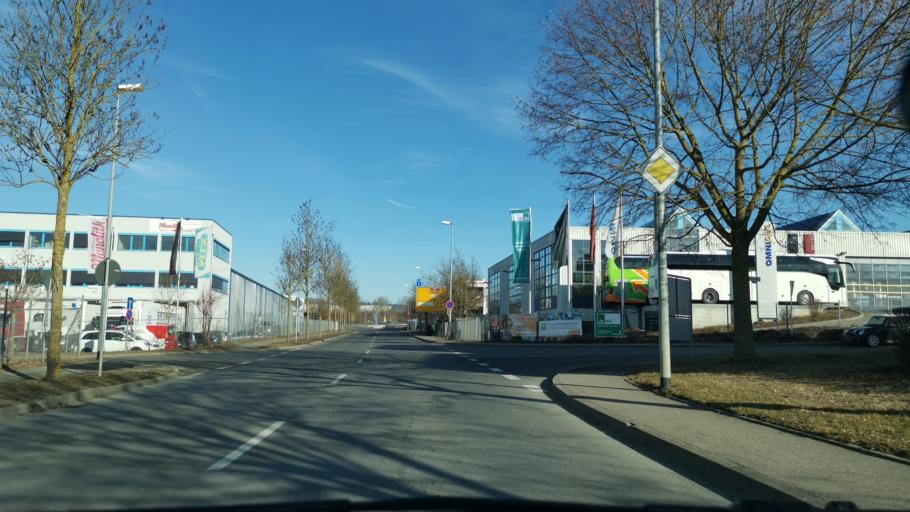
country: DE
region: Baden-Wuerttemberg
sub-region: Regierungsbezirk Stuttgart
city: Herrenberg
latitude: 48.5760
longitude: 8.8932
